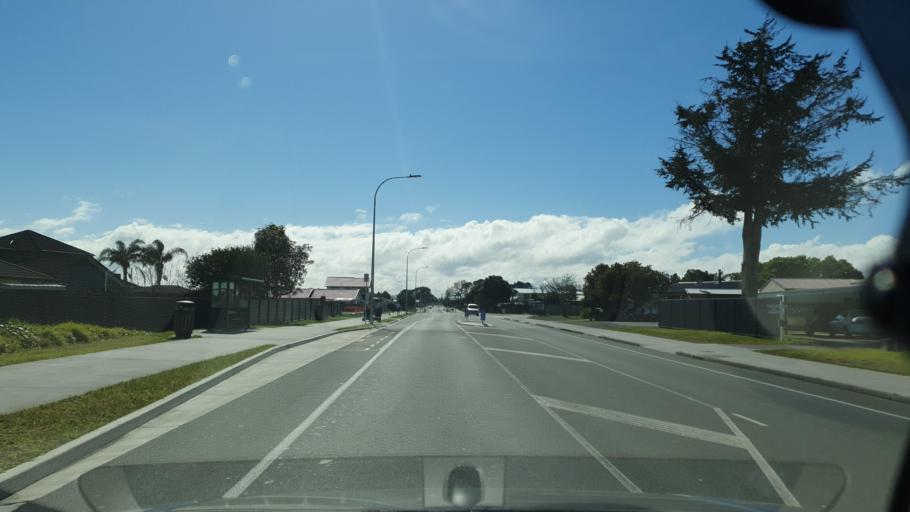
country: NZ
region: Bay of Plenty
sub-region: Tauranga City
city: Tauranga
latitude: -37.7061
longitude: 176.2847
